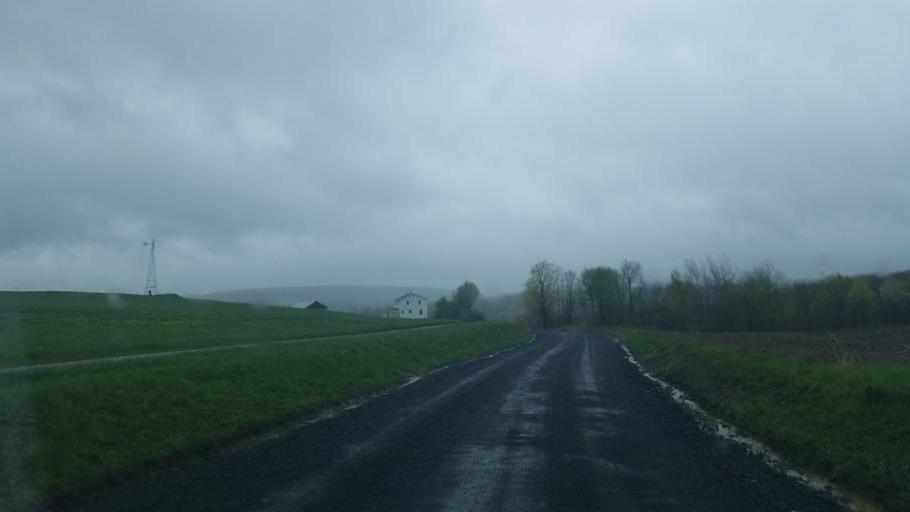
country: US
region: New York
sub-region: Allegany County
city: Andover
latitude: 41.9403
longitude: -77.7695
